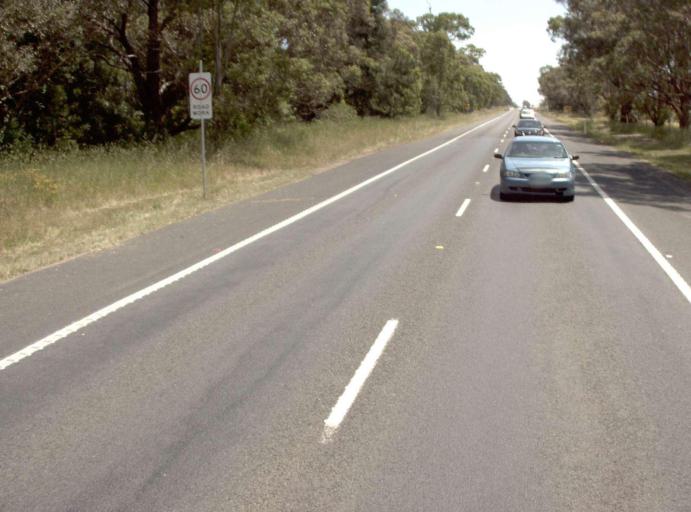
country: AU
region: Victoria
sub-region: Latrobe
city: Traralgon
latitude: -38.1841
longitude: 146.6002
